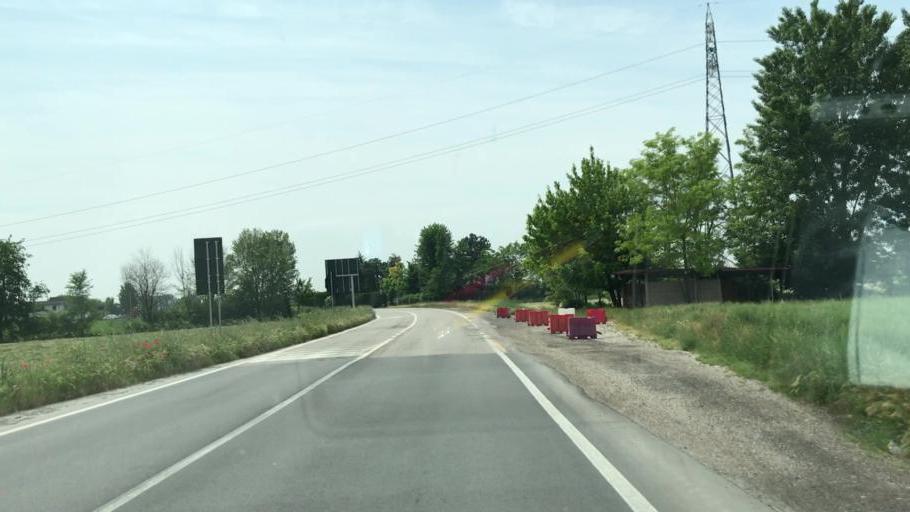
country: IT
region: Lombardy
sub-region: Provincia di Mantova
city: Campitello
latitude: 45.0825
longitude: 10.5986
